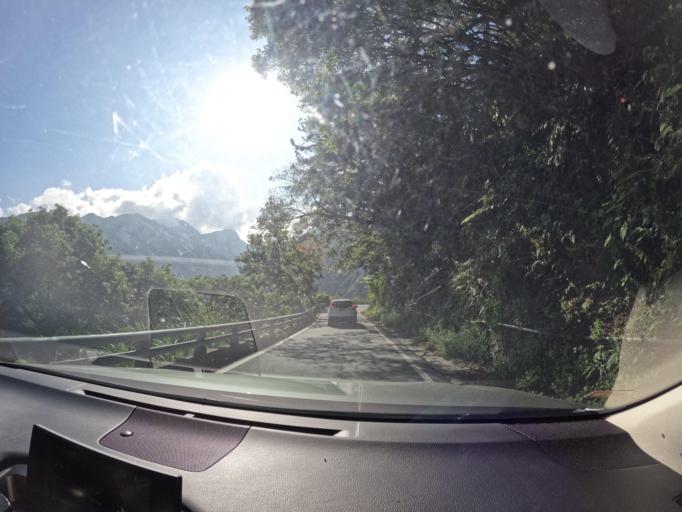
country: TW
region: Taiwan
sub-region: Taitung
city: Taitung
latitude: 23.2003
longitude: 121.0200
